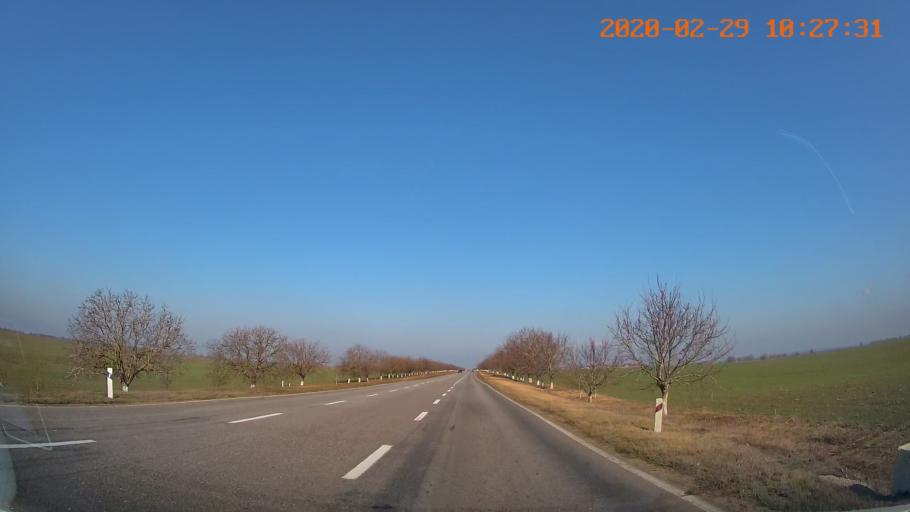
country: MD
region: Telenesti
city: Tiraspolul Nou
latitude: 46.8971
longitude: 29.5973
